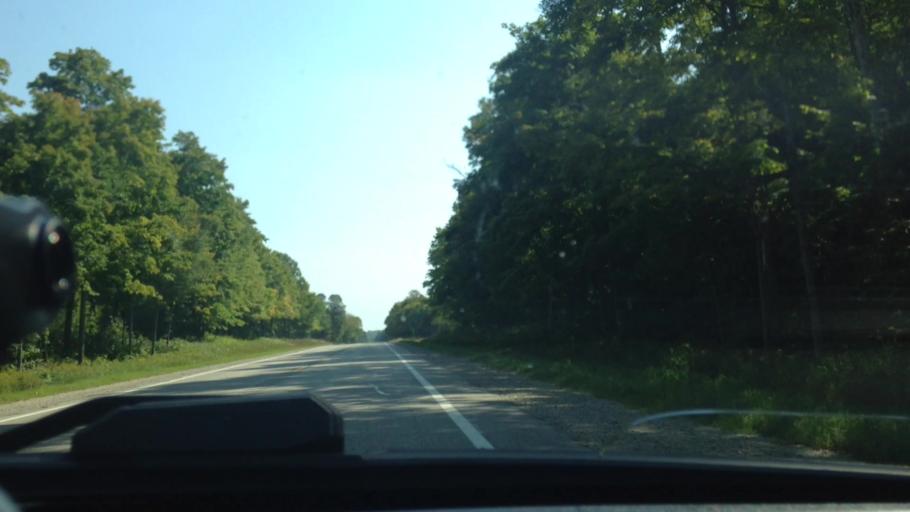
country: US
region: Michigan
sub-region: Luce County
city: Newberry
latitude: 46.3222
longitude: -85.6688
